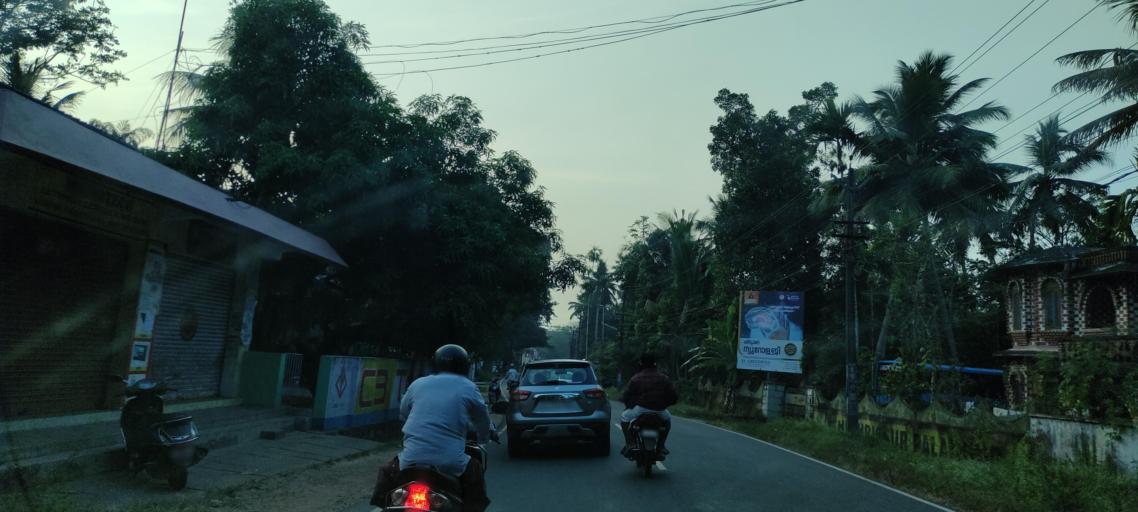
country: IN
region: Kerala
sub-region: Alappuzha
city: Mavelikara
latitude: 9.2781
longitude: 76.5355
